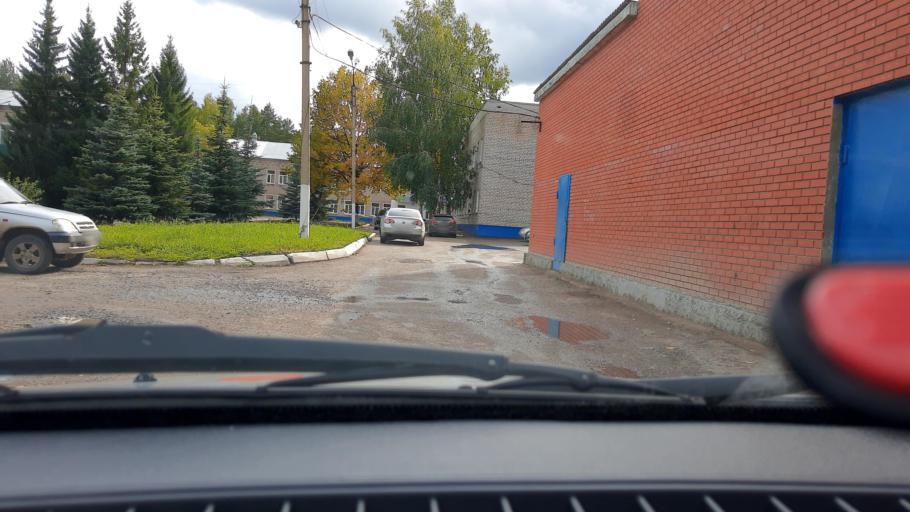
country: RU
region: Bashkortostan
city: Belebey
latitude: 54.1033
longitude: 54.0944
